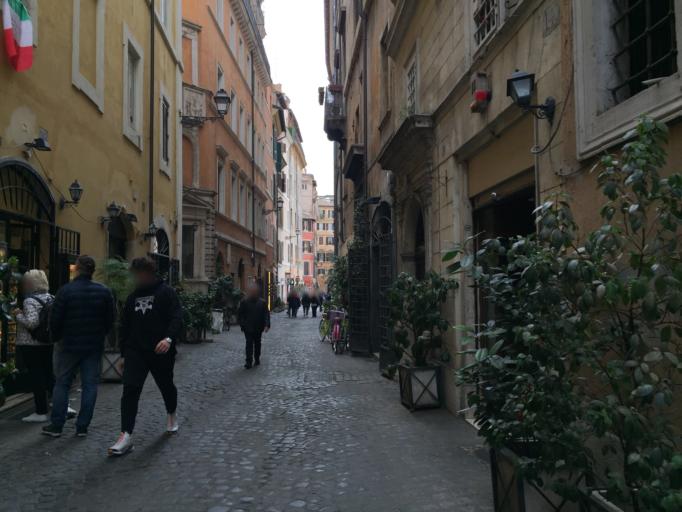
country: VA
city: Vatican City
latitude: 41.9005
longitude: 12.4684
